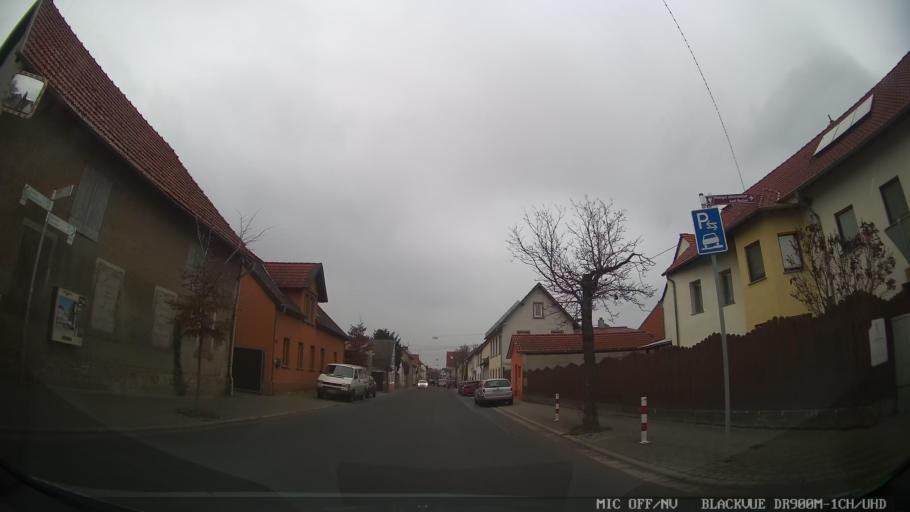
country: DE
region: Rheinland-Pfalz
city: Gau-Odernheim
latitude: 49.7817
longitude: 8.1965
